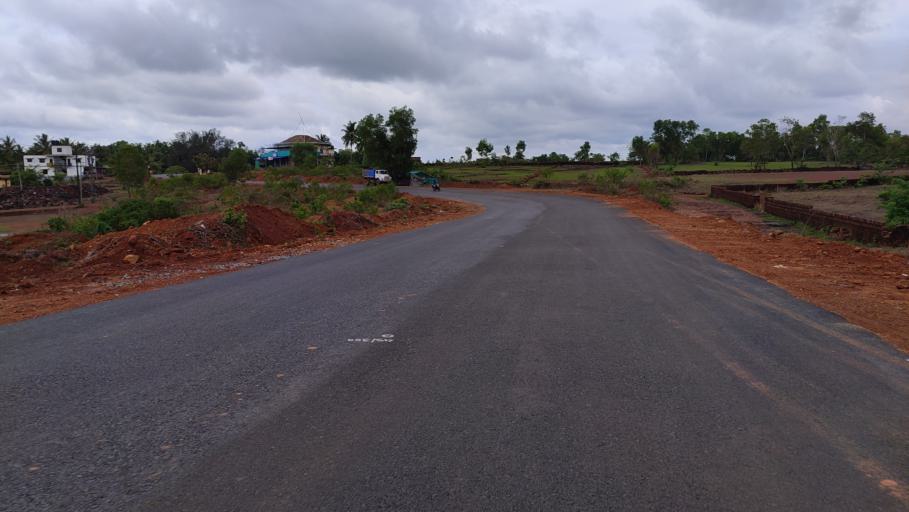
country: IN
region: Kerala
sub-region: Kasaragod District
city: Kasaragod
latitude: 12.5501
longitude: 75.0709
